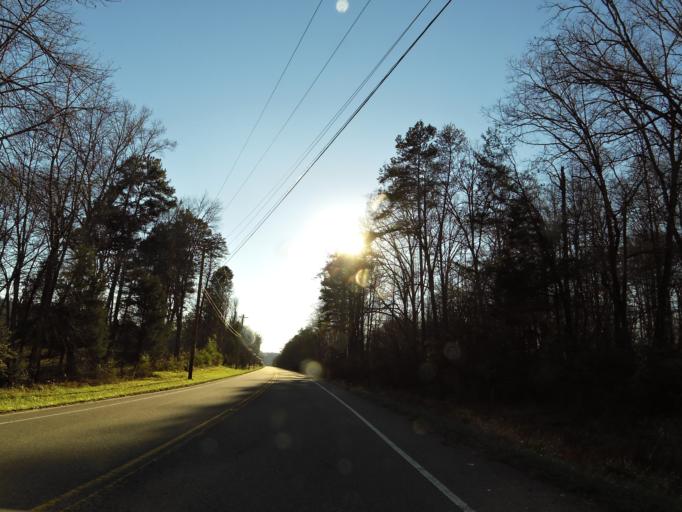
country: US
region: Tennessee
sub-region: Anderson County
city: Oak Ridge
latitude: 36.0591
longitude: -84.2354
